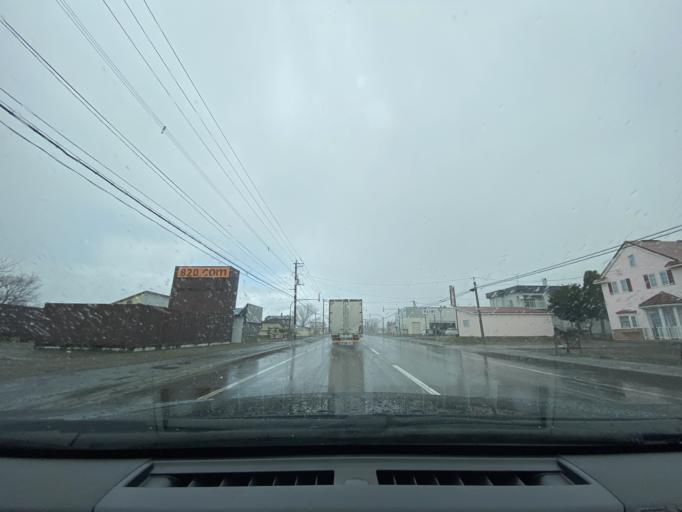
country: JP
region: Hokkaido
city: Takikawa
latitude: 43.6312
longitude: 141.9439
